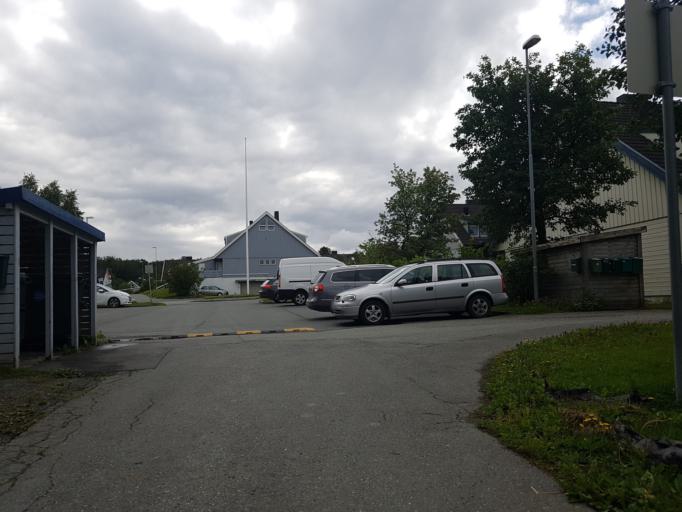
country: NO
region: Sor-Trondelag
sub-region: Trondheim
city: Trondheim
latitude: 63.3845
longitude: 10.4051
